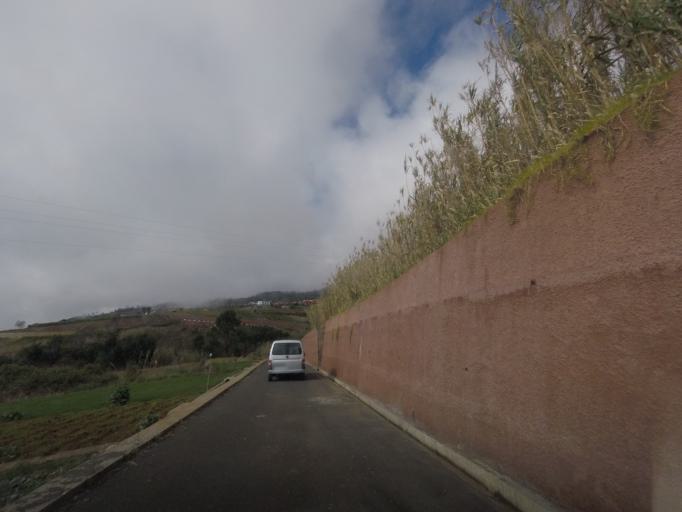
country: PT
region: Madeira
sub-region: Calheta
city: Faja da Ovelha
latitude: 32.7644
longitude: -17.2205
